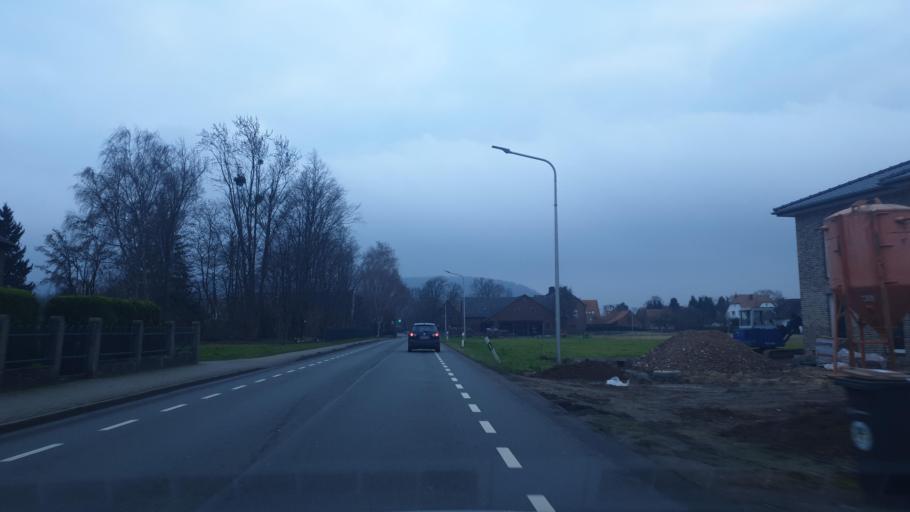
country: DE
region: North Rhine-Westphalia
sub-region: Regierungsbezirk Detmold
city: Minden
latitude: 52.2657
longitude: 8.9289
